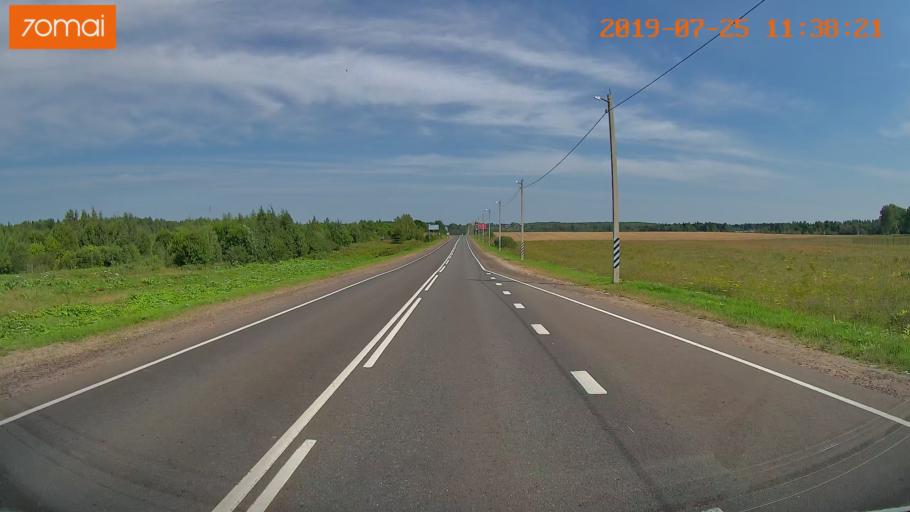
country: RU
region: Ivanovo
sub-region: Privolzhskiy Rayon
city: Ples
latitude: 57.4406
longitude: 41.4816
